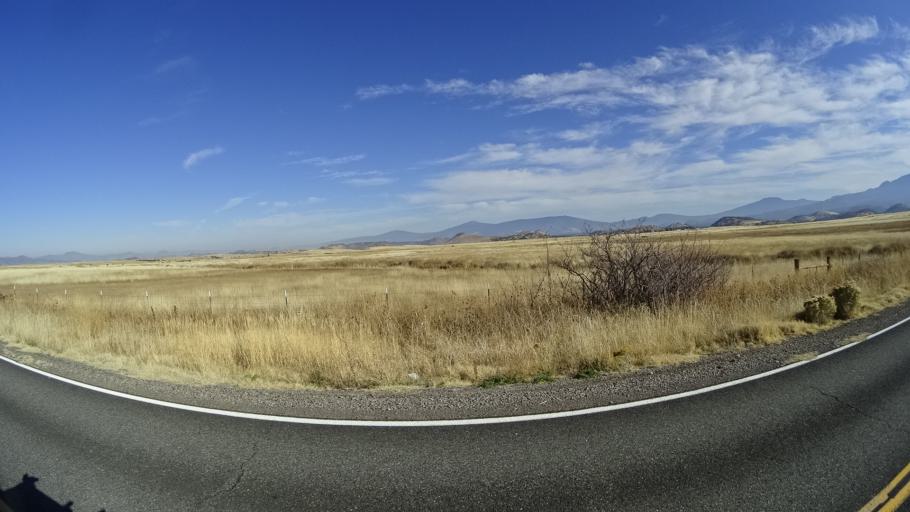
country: US
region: California
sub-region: Siskiyou County
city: Weed
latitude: 41.4698
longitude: -122.4744
